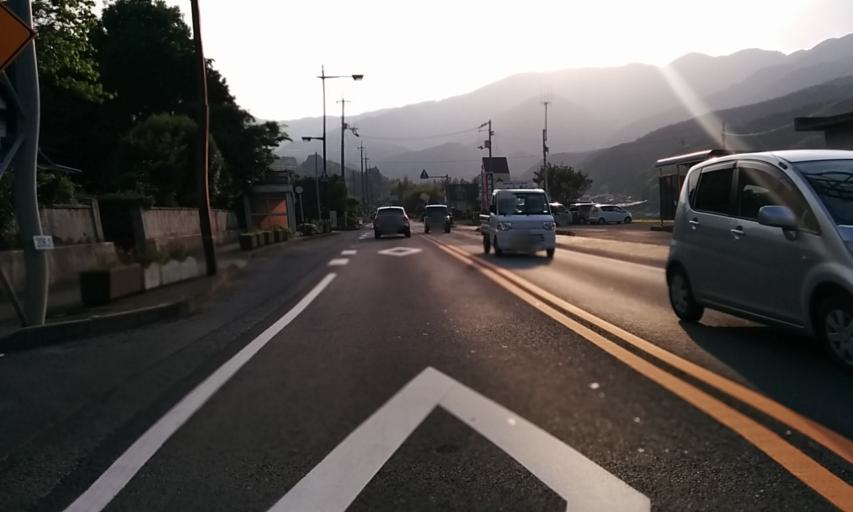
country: JP
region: Ehime
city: Saijo
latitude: 33.8568
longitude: 133.0188
